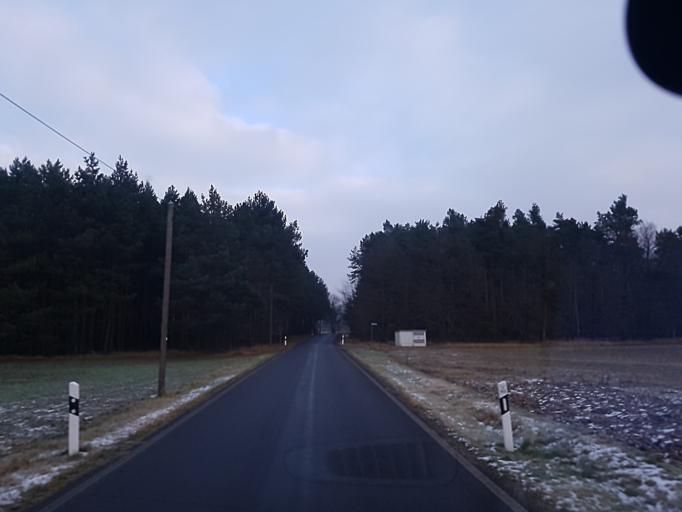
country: DE
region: Brandenburg
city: Crinitz
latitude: 51.7412
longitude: 13.8308
